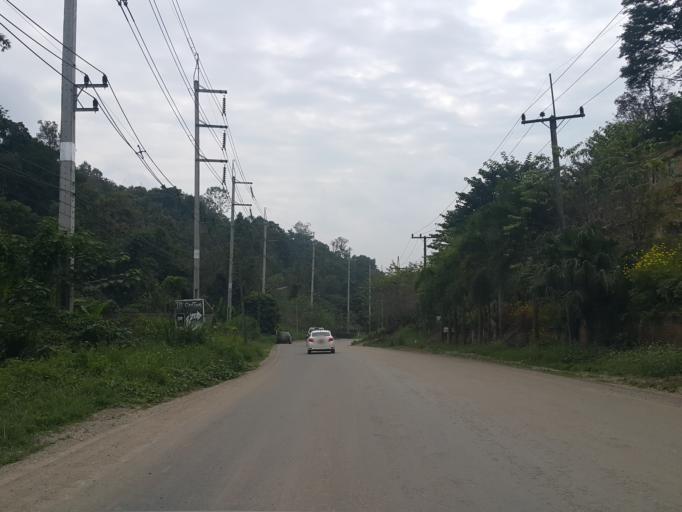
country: TH
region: Chiang Mai
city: Mae Taeng
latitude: 19.1691
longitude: 98.6913
